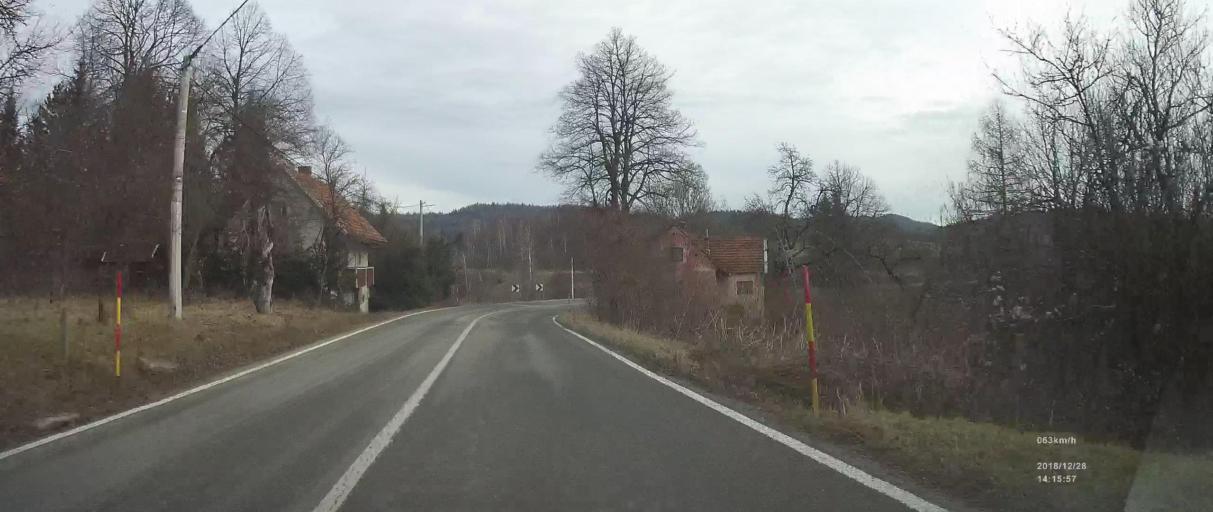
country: HR
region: Primorsko-Goranska
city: Vrbovsko
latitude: 45.4218
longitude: 15.0317
